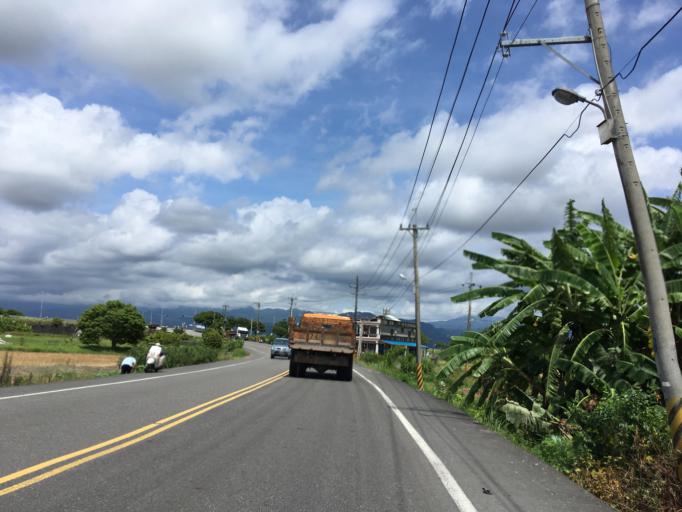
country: TW
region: Taiwan
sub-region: Yilan
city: Yilan
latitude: 24.7032
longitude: 121.7583
